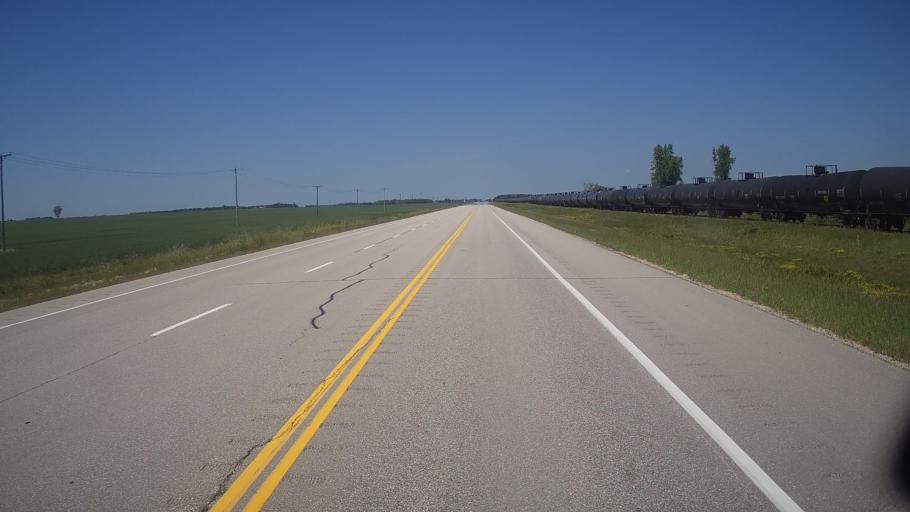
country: CA
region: Manitoba
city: Stonewall
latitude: 50.0937
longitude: -97.4876
